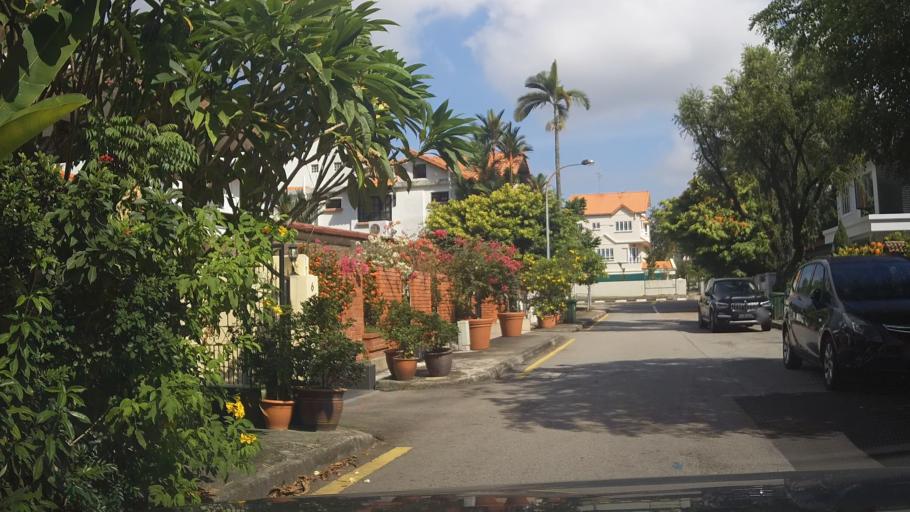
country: SG
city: Singapore
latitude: 1.3137
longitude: 103.9365
